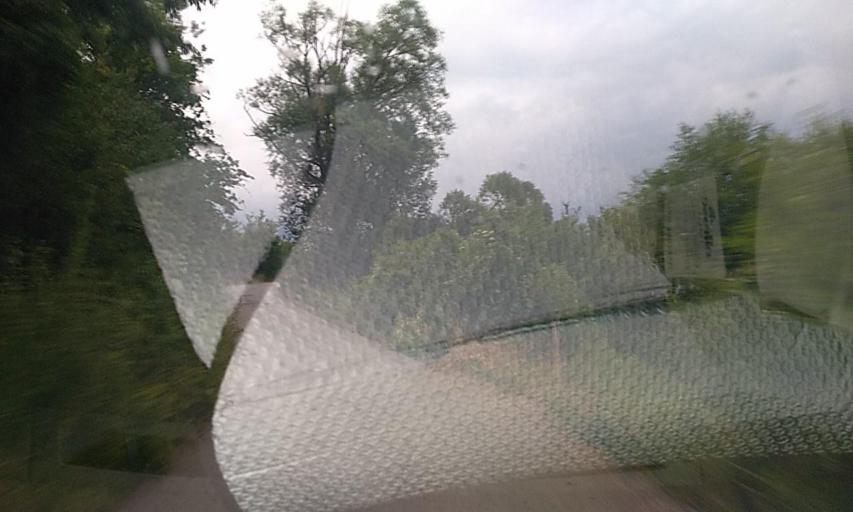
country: RS
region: Central Serbia
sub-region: Pirotski Okrug
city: Bela Palanka
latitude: 43.2458
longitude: 22.1928
